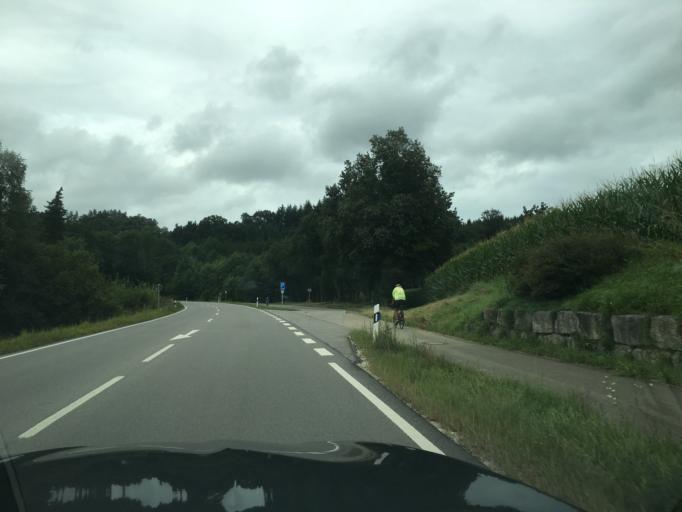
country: DE
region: Bavaria
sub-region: Swabia
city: Zusmarshausen
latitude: 48.4201
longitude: 10.5997
